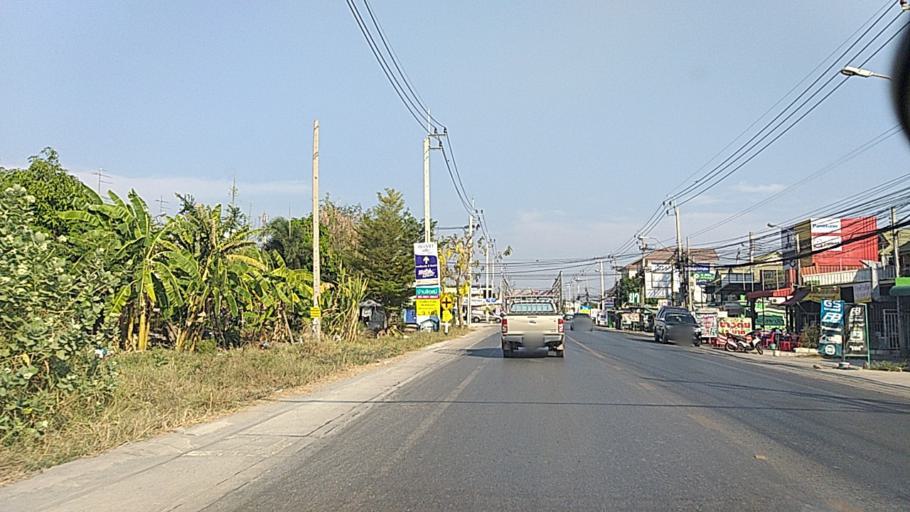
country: TH
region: Nonthaburi
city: Bang Bua Thong
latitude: 13.9314
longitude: 100.3761
